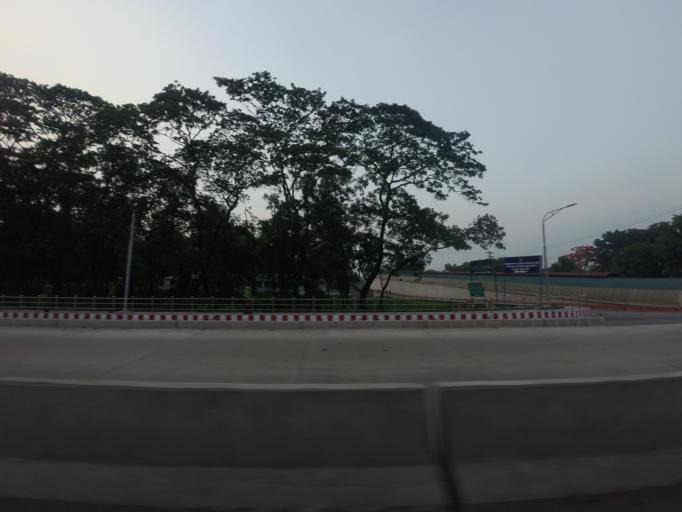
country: BD
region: Chittagong
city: Comilla
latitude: 23.4788
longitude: 91.1123
